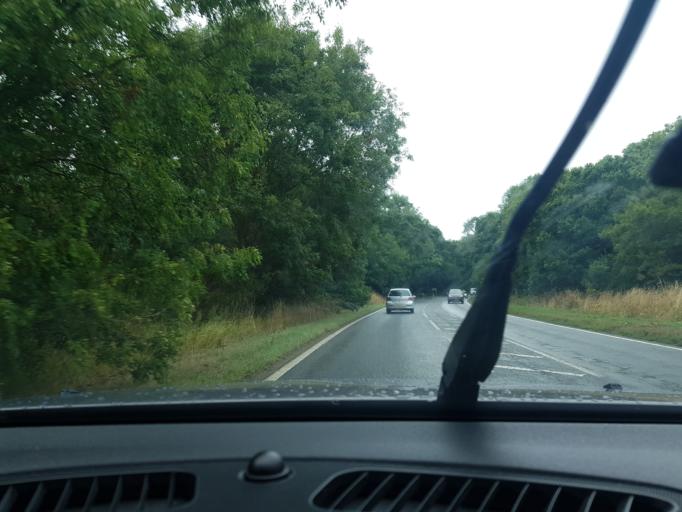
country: GB
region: England
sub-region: Hampshire
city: Odiham
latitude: 51.2470
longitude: -0.8921
